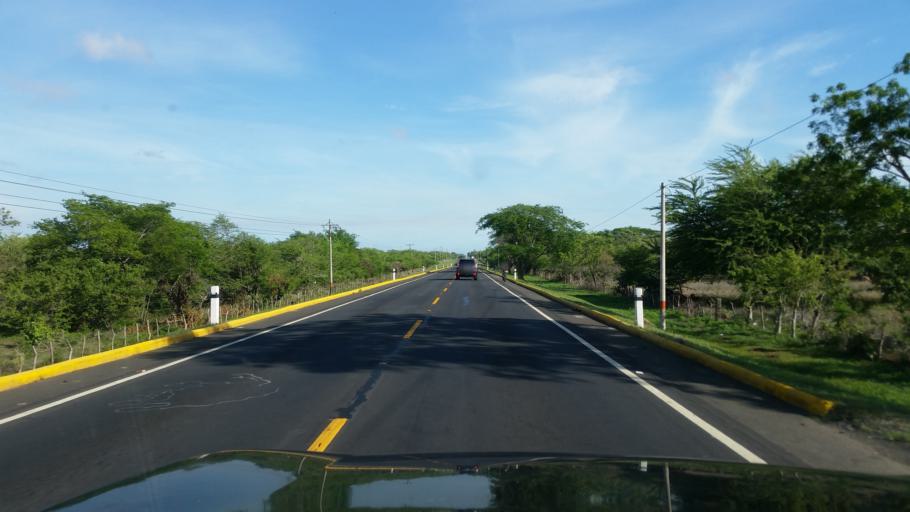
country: NI
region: Leon
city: La Paz Centro
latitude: 12.2708
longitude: -86.7397
